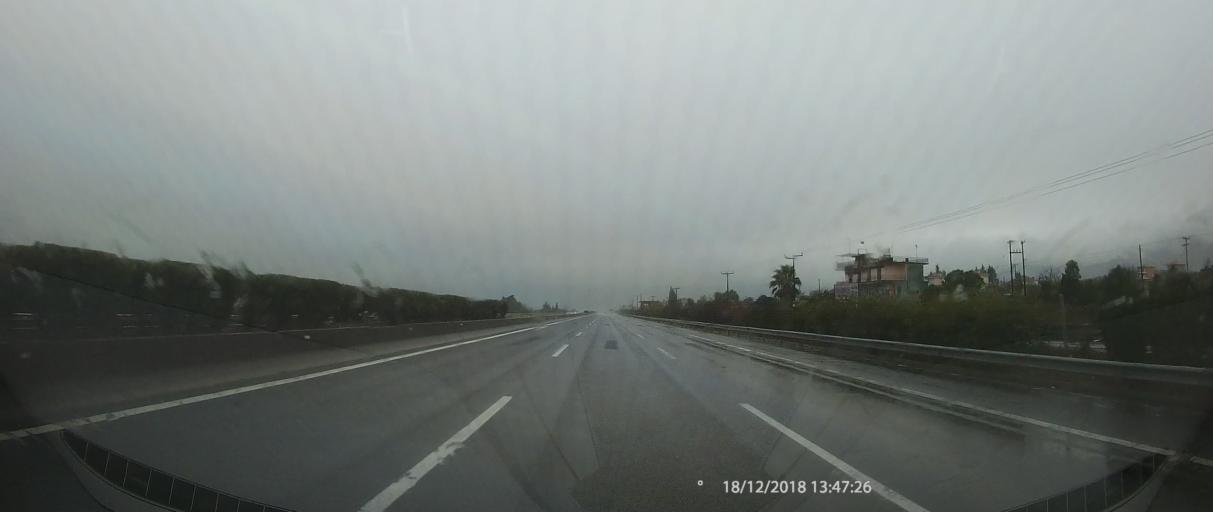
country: GR
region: Central Macedonia
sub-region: Nomos Pierias
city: Leptokarya
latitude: 40.0763
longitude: 22.5547
